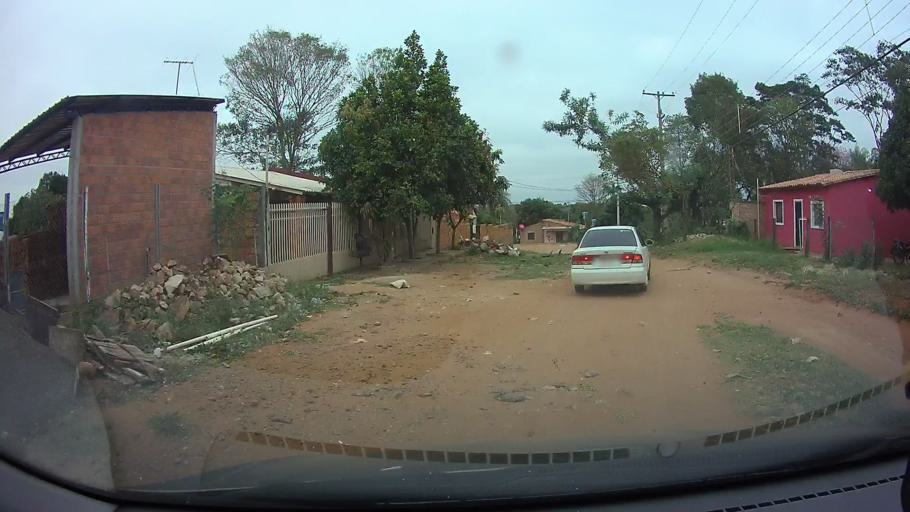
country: PY
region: Central
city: Limpio
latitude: -25.1532
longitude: -57.4556
